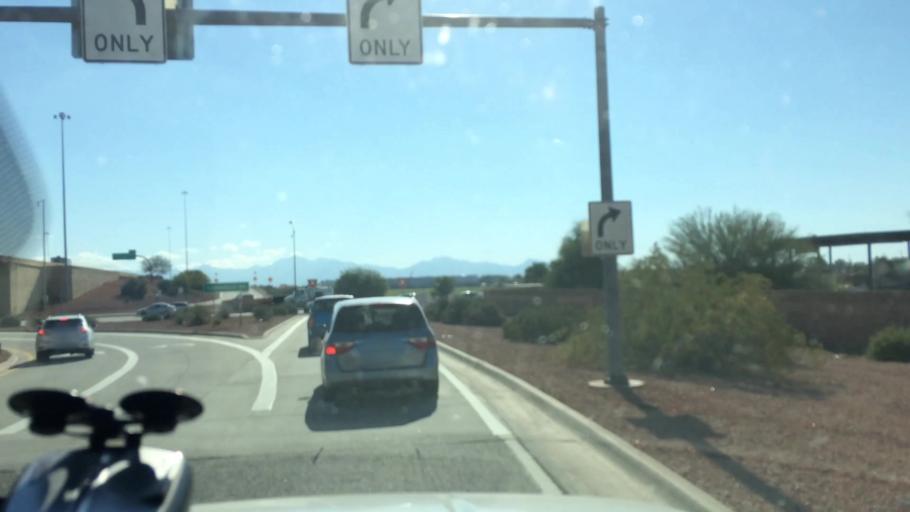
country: US
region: Arizona
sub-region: Maricopa County
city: Tolleson
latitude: 33.5094
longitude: -112.2698
